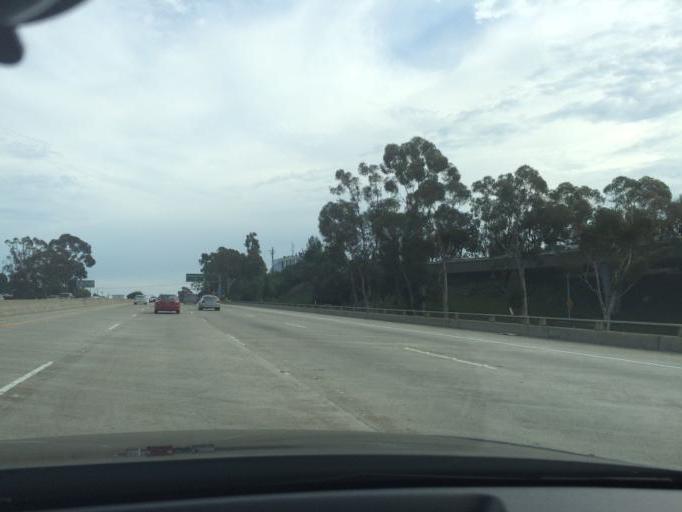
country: US
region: California
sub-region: San Diego County
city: San Diego
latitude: 32.8096
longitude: -117.1527
